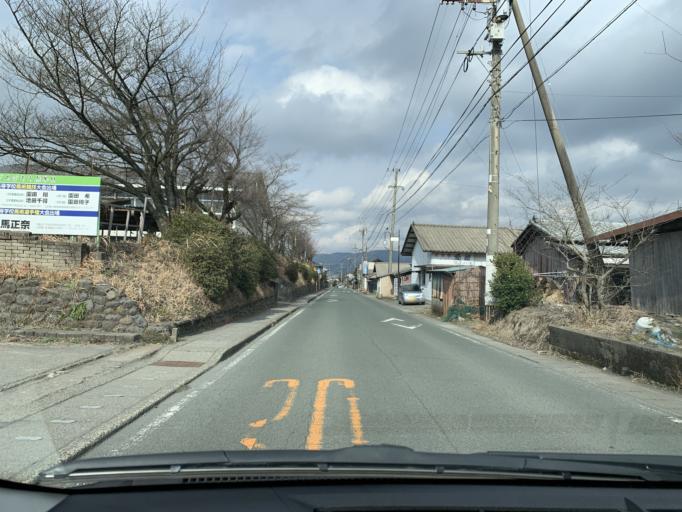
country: JP
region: Kumamoto
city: Aso
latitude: 32.9414
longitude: 131.1156
